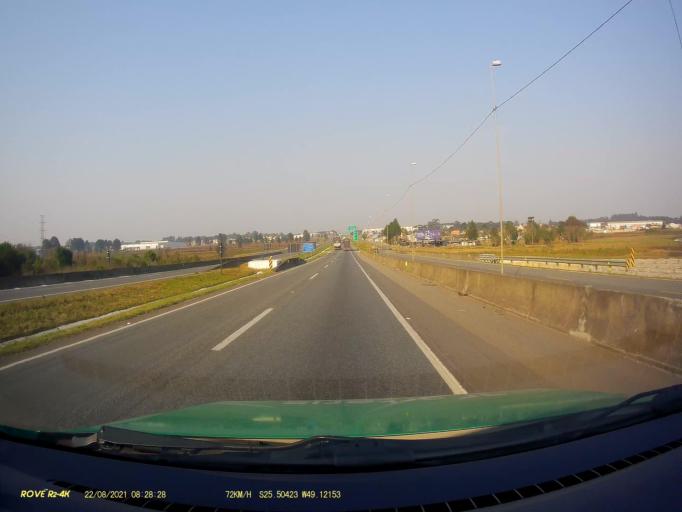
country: BR
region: Parana
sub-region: Piraquara
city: Piraquara
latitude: -25.5044
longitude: -49.1217
